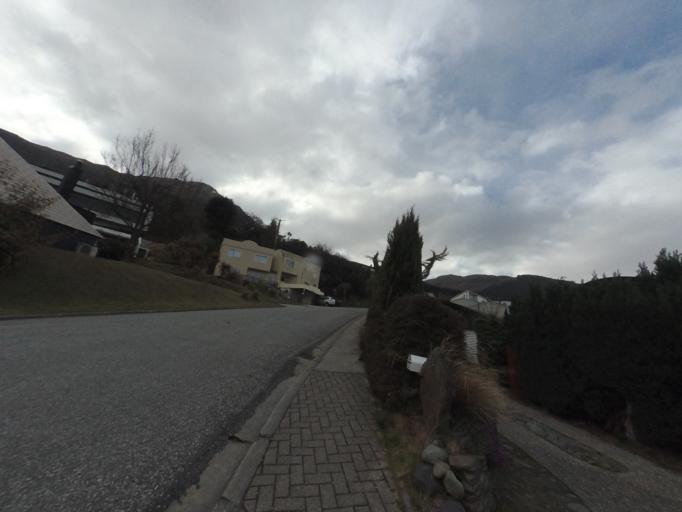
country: NZ
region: Otago
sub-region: Queenstown-Lakes District
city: Queenstown
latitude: -45.0408
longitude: 168.6335
